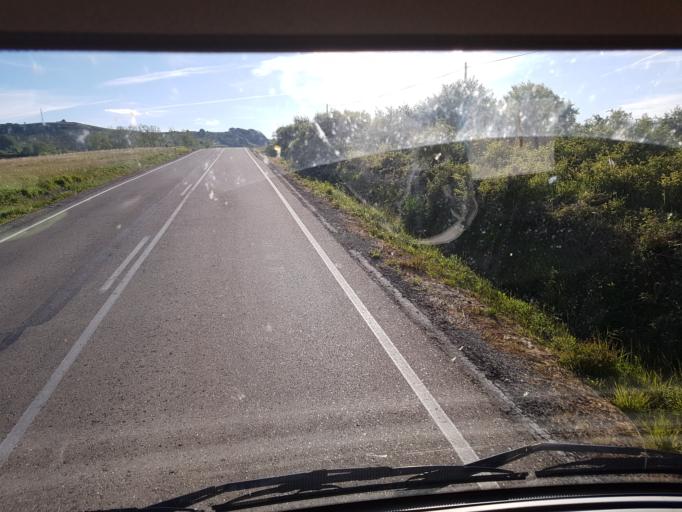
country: ES
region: Castille and Leon
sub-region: Provincia de Burgos
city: Arija
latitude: 42.9766
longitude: -3.8758
